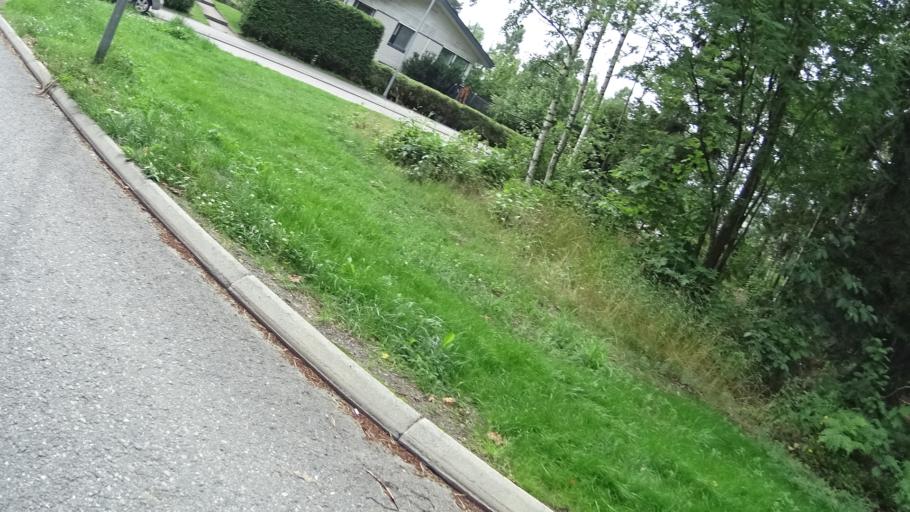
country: FI
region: Uusimaa
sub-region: Helsinki
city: Teekkarikylae
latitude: 60.2219
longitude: 24.8375
